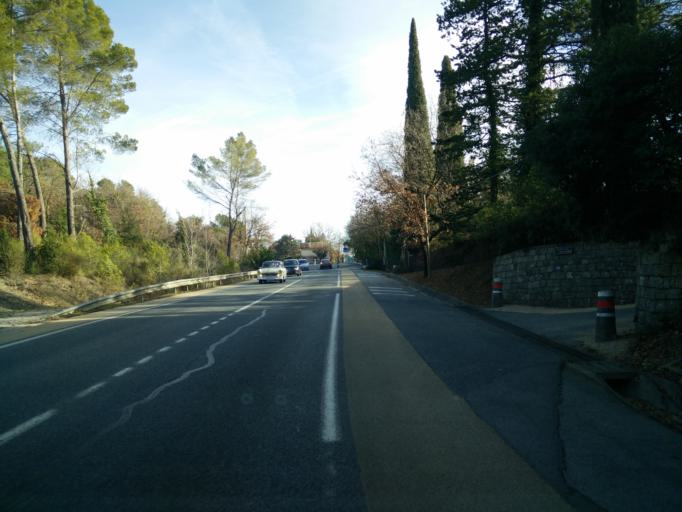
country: FR
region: Provence-Alpes-Cote d'Azur
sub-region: Departement du Var
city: Montauroux
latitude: 43.5983
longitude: 6.7885
